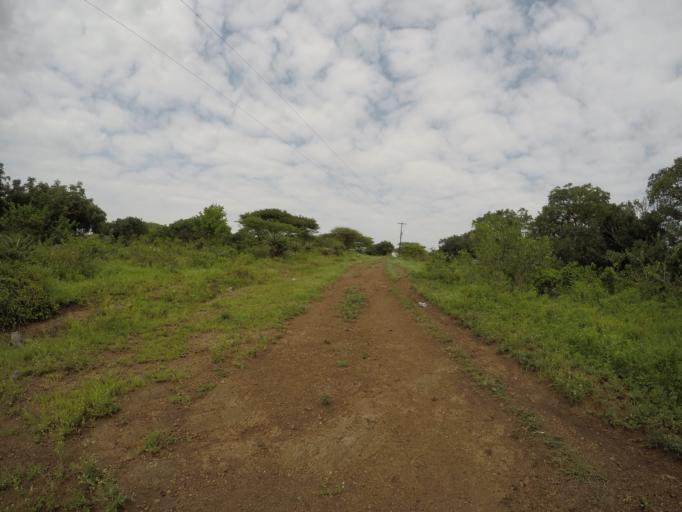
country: ZA
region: KwaZulu-Natal
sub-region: uThungulu District Municipality
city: Empangeni
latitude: -28.6260
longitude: 31.9114
